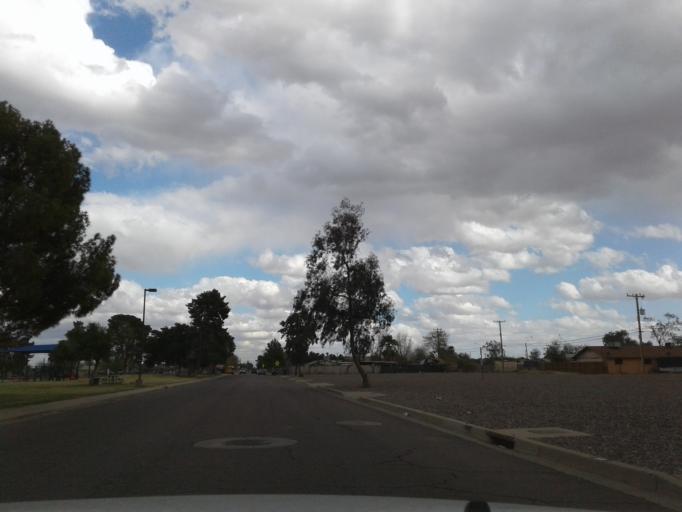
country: US
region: Arizona
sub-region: Maricopa County
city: Phoenix
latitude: 33.4332
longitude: -112.0636
